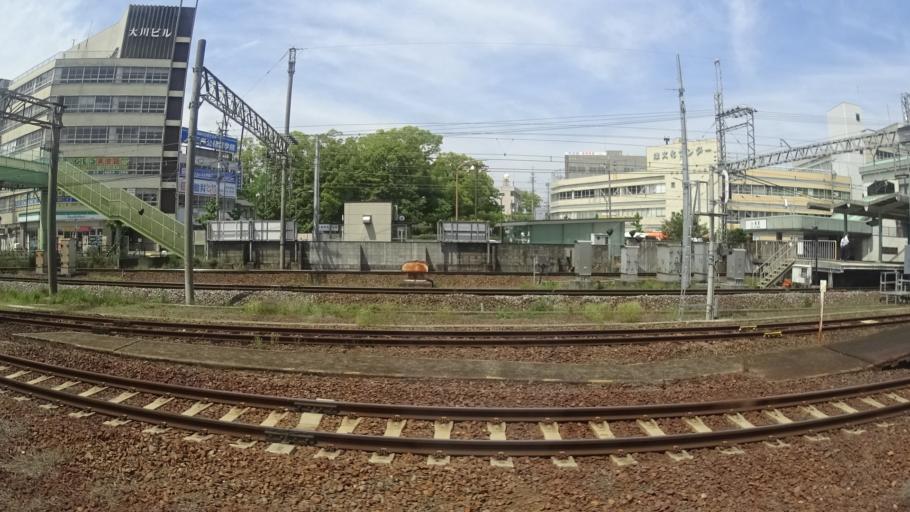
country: JP
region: Mie
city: Tsu-shi
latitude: 34.7332
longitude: 136.5107
